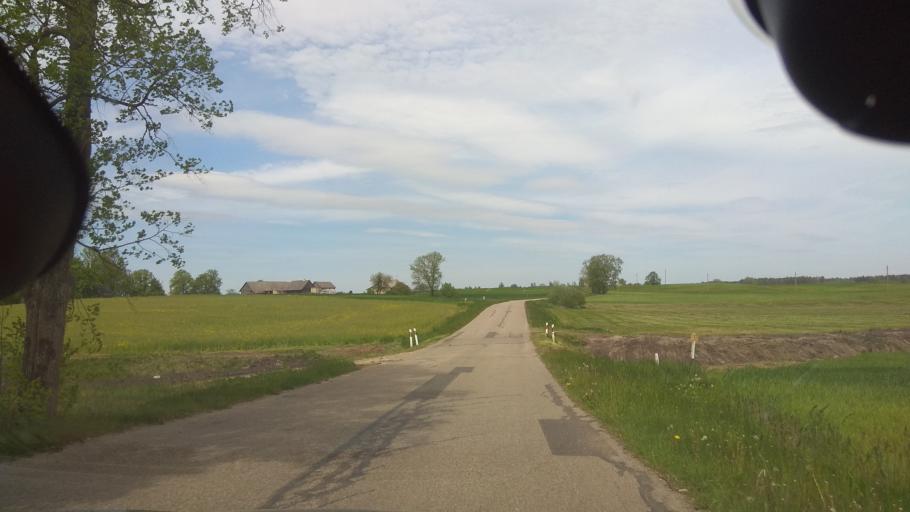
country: LT
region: Vilnius County
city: Ukmerge
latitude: 55.1536
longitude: 24.5446
